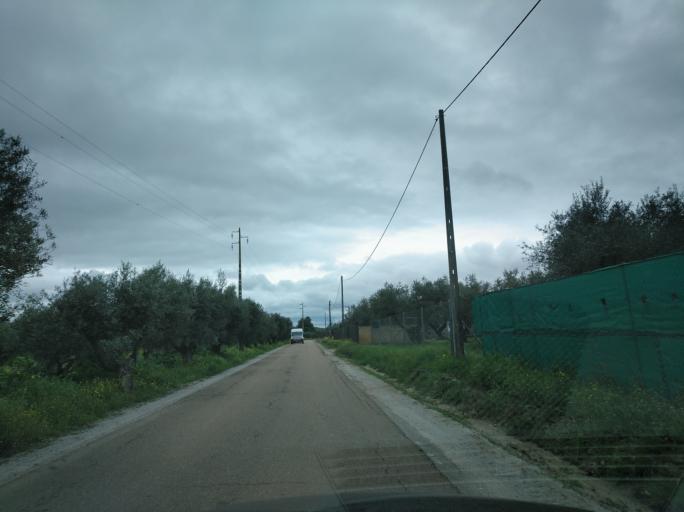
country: PT
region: Portalegre
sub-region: Campo Maior
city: Campo Maior
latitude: 38.9979
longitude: -7.0525
